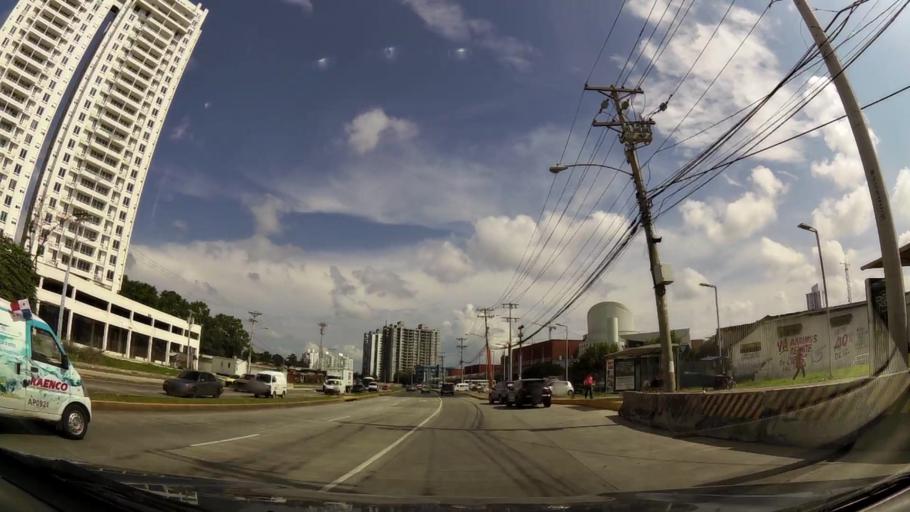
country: PA
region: Panama
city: Panama
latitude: 9.0084
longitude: -79.5187
